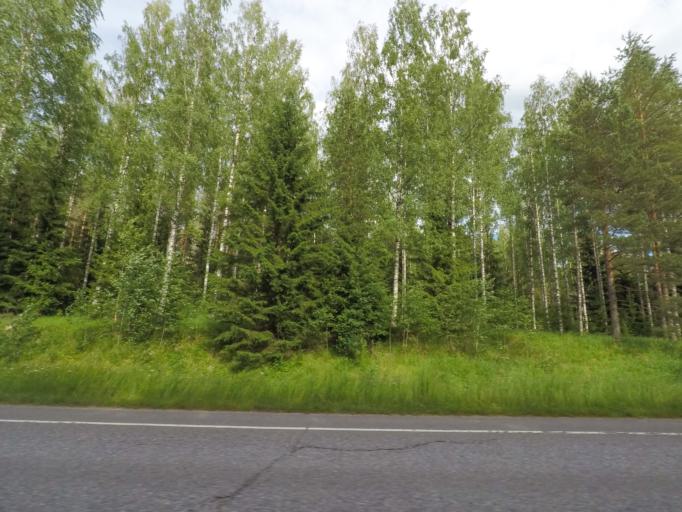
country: FI
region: Paijanne Tavastia
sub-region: Lahti
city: Hollola
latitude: 60.8425
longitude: 25.4944
